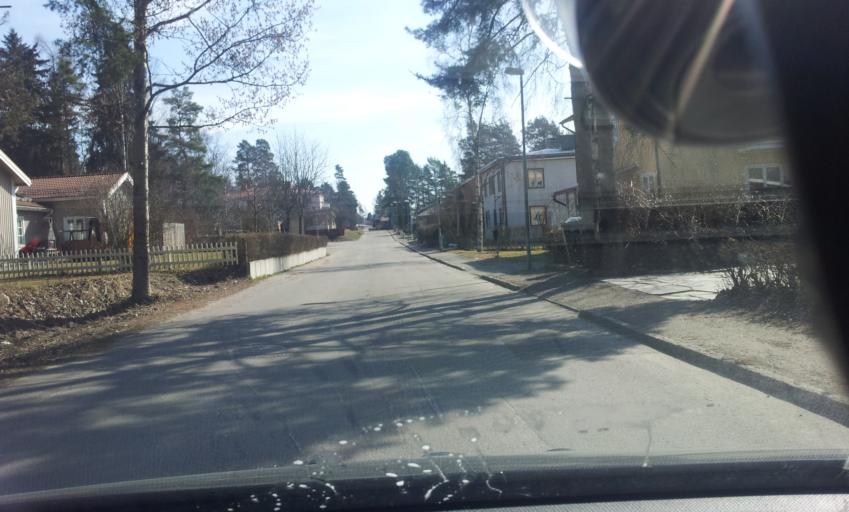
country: SE
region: Gaevleborg
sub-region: Ljusdals Kommun
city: Ljusdal
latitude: 61.8289
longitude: 16.1062
